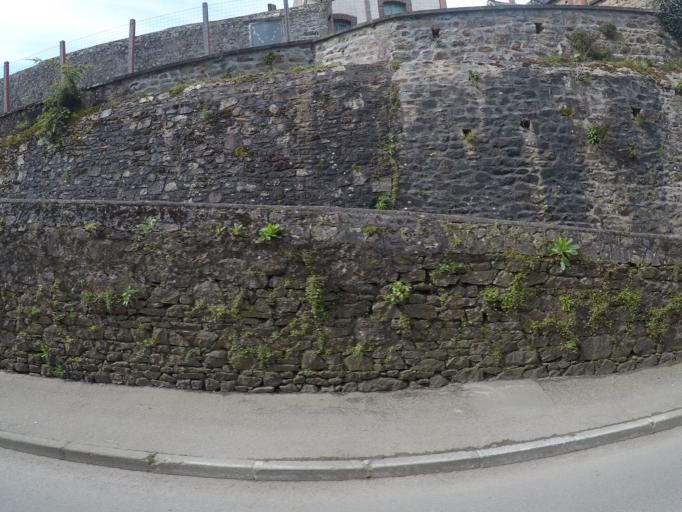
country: FR
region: Brittany
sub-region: Departement des Cotes-d'Armor
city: Plelo
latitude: 48.5408
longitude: -2.9706
